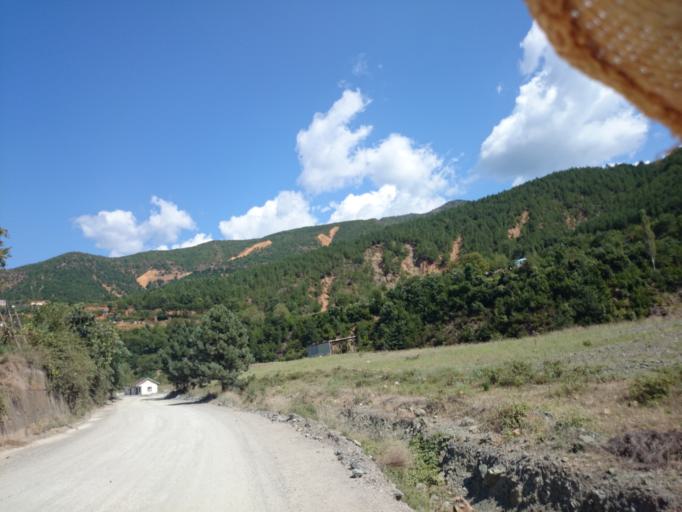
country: AL
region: Lezhe
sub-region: Rrethi i Lezhes
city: Blinisht
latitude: 41.8631
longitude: 20.0153
